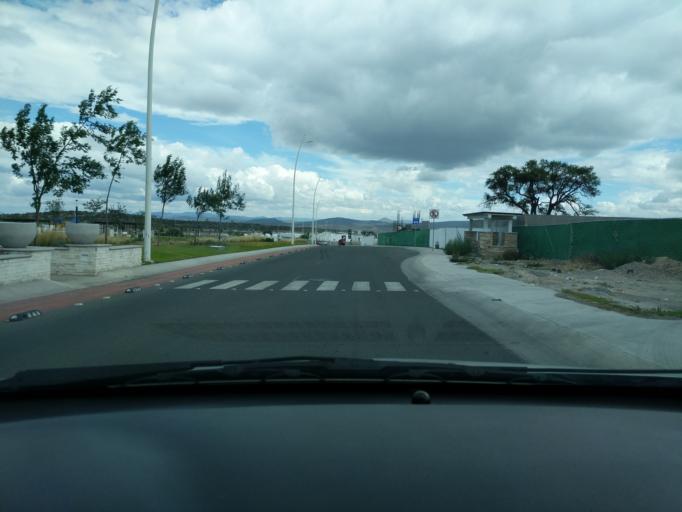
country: MX
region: Queretaro
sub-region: El Marques
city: El Pozo
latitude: 20.6526
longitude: -100.3145
